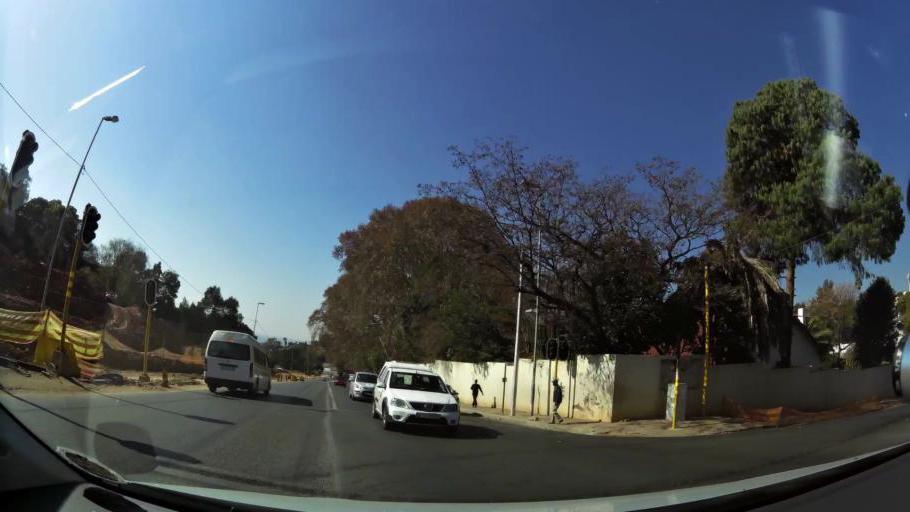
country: ZA
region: Gauteng
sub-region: City of Johannesburg Metropolitan Municipality
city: Johannesburg
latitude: -26.1720
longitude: 28.0709
